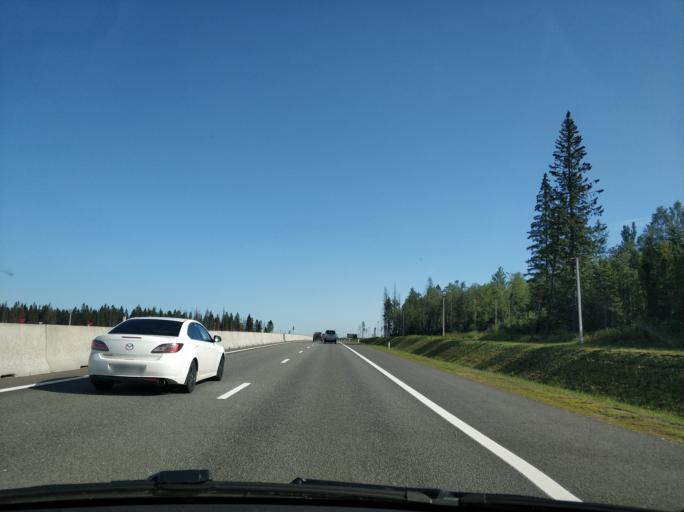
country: RU
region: Leningrad
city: Sosnovo
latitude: 60.4896
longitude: 30.1958
